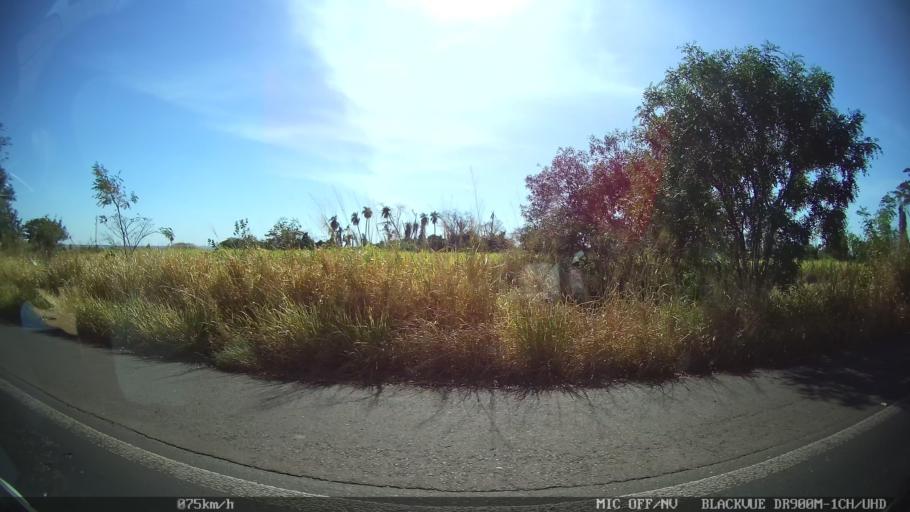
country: BR
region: Sao Paulo
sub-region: Barretos
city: Barretos
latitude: -20.5752
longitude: -48.6793
